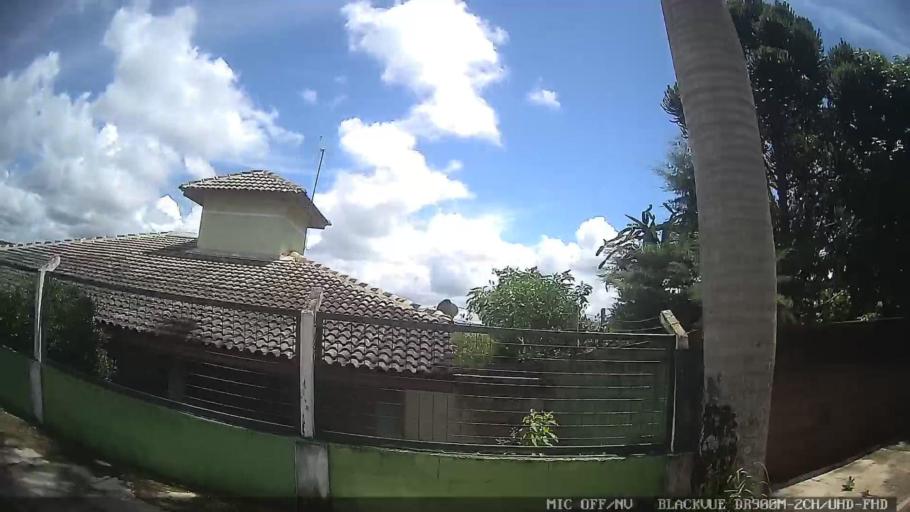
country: BR
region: Sao Paulo
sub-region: Amparo
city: Amparo
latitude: -22.8186
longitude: -46.6918
